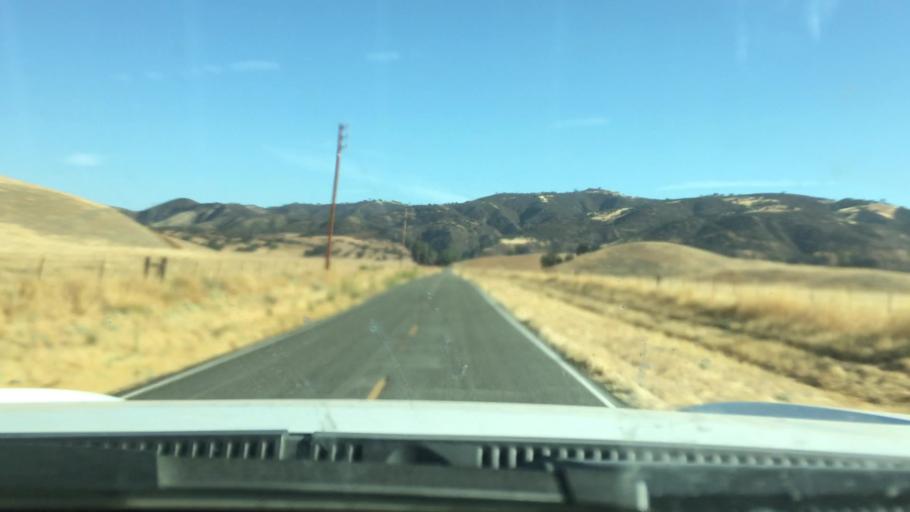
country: US
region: California
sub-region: Monterey County
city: King City
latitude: 36.3951
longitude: -121.0001
